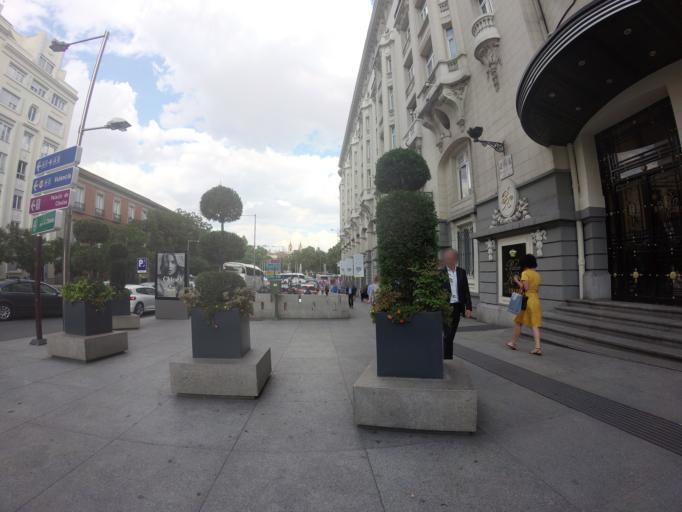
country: ES
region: Madrid
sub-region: Provincia de Madrid
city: Madrid
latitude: 40.4156
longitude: -3.6956
